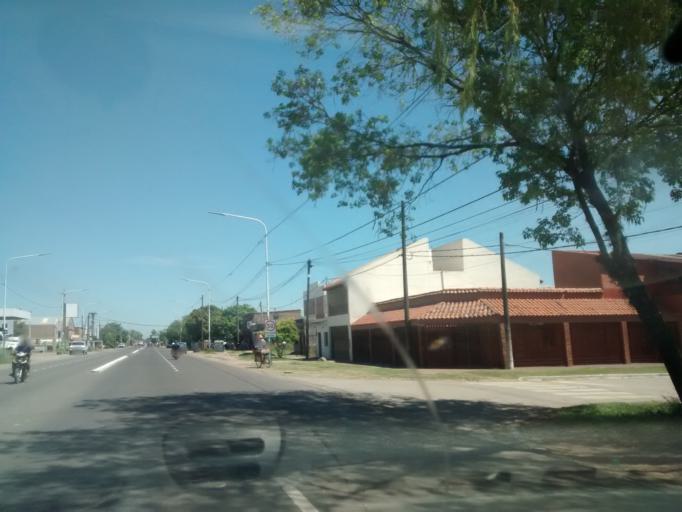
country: AR
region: Chaco
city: Fontana
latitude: -27.4273
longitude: -59.0278
